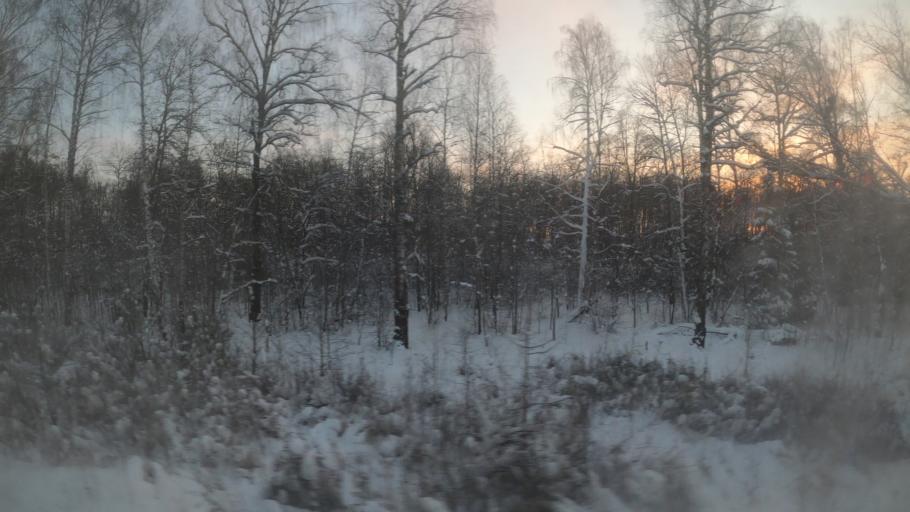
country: RU
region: Moskovskaya
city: Podosinki
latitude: 56.2124
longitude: 37.5268
